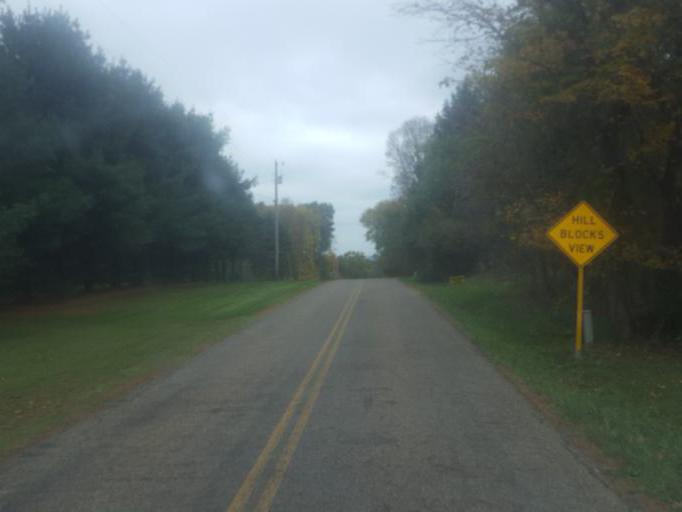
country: US
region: Ohio
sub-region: Richland County
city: Lincoln Heights
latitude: 40.7416
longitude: -82.4038
